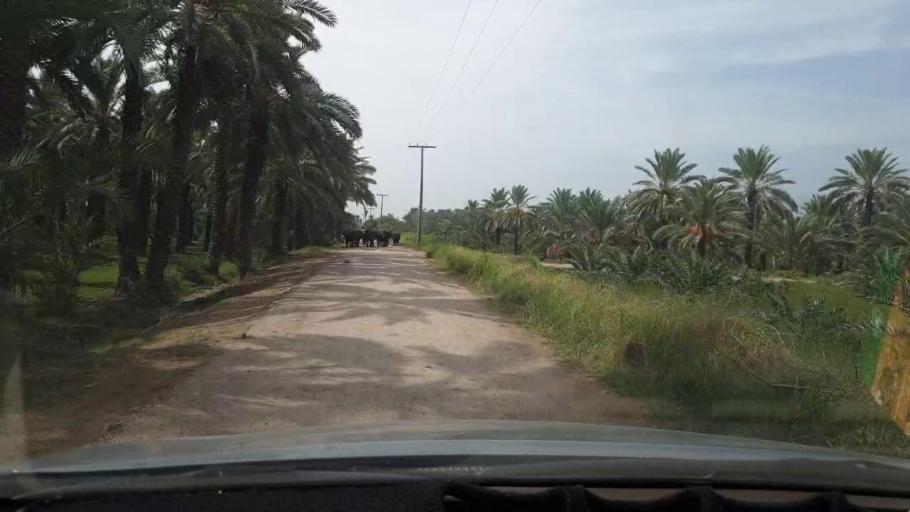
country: PK
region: Sindh
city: Khairpur
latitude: 27.4966
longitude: 68.7545
